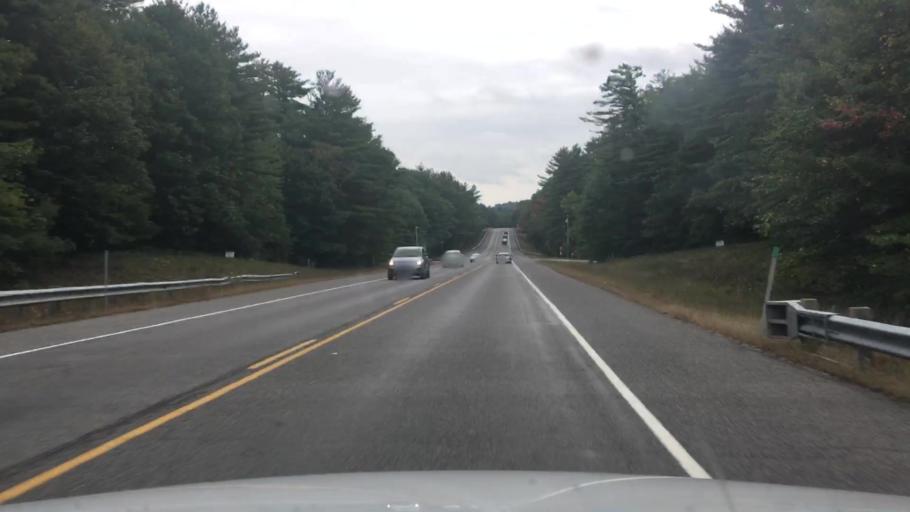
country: US
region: New Hampshire
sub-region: Carroll County
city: Wolfeboro
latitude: 43.4988
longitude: -71.2605
